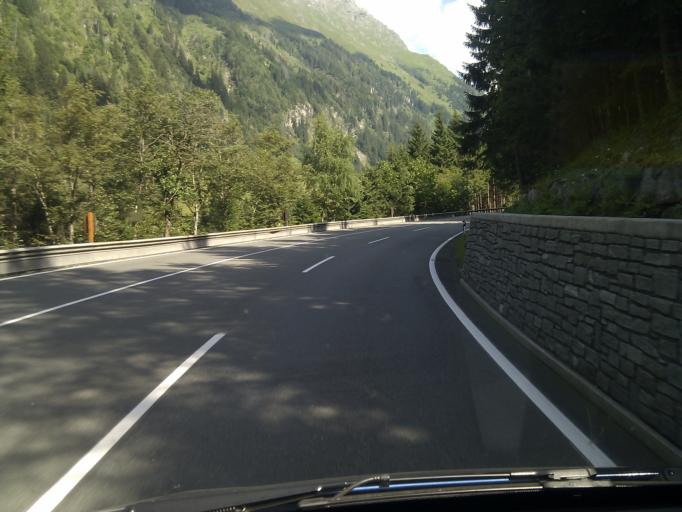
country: AT
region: Salzburg
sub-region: Politischer Bezirk Zell am See
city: Mittersill
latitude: 47.2237
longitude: 12.4925
